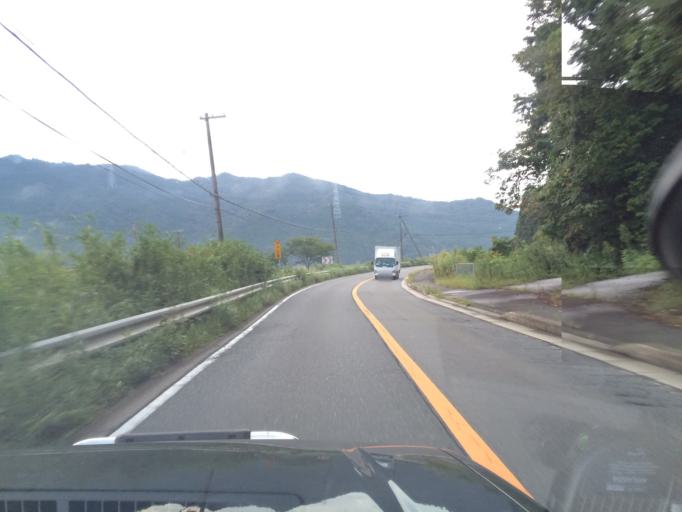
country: JP
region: Hyogo
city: Nishiwaki
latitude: 35.1101
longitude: 134.9950
